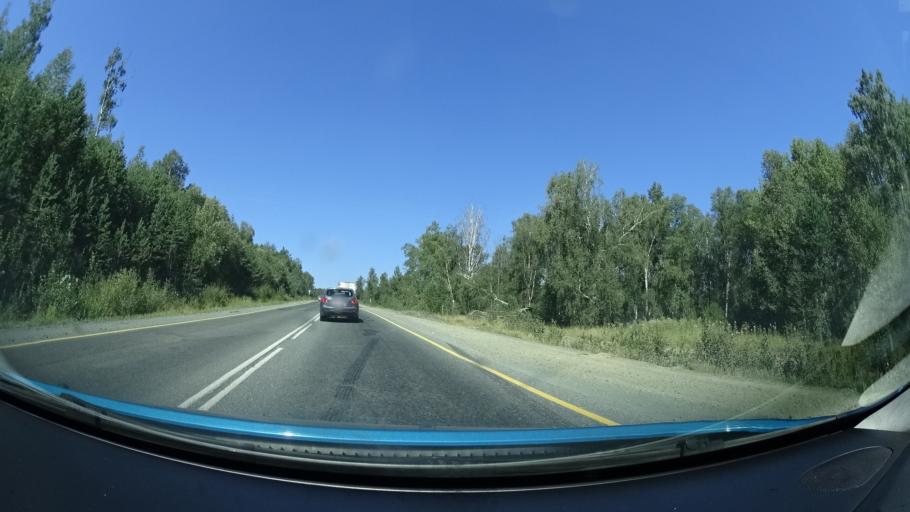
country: RU
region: Bashkortostan
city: Abzakovo
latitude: 53.8898
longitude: 58.5225
